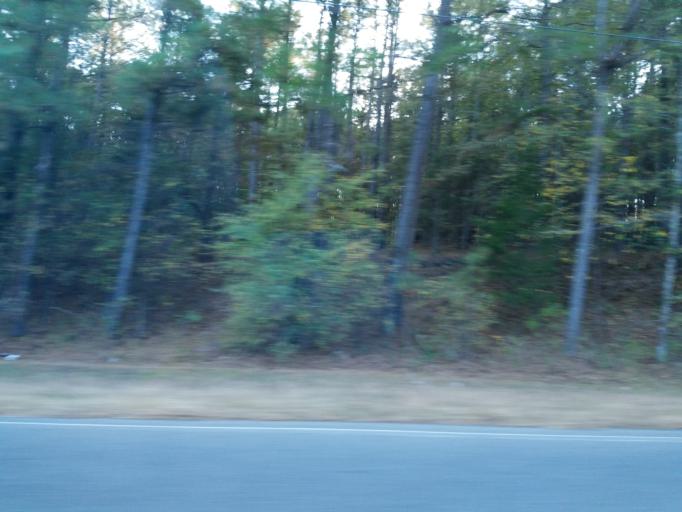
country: US
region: Georgia
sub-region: Bartow County
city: Euharlee
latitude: 34.2422
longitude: -84.9548
